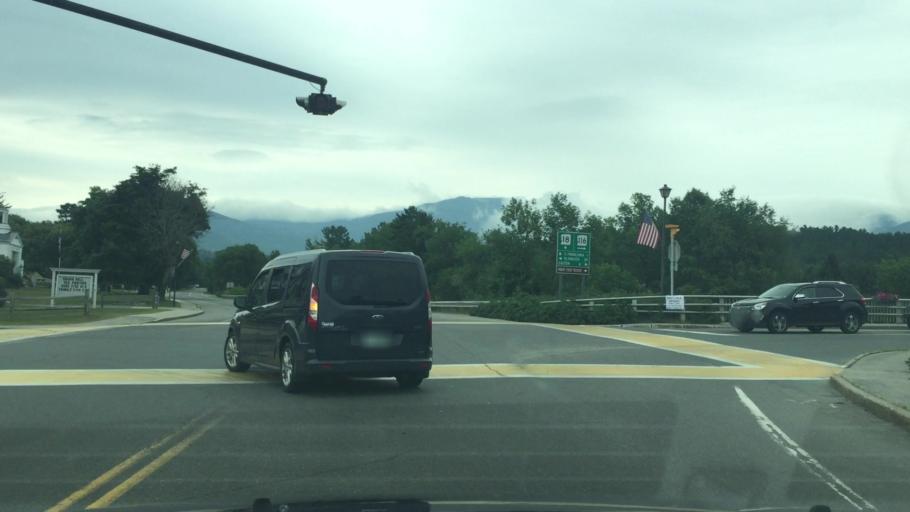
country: US
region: New Hampshire
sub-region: Grafton County
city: Littleton
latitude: 44.2273
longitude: -71.7480
